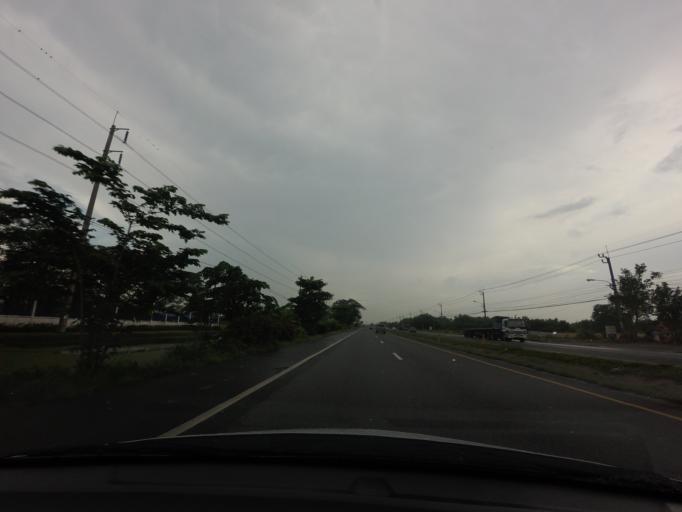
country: TH
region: Bangkok
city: Nong Chok
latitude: 13.8106
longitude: 100.9158
